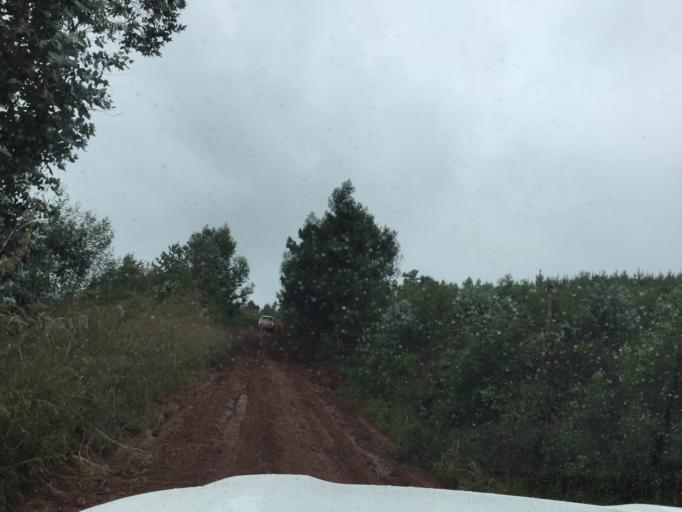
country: TZ
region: Iringa
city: Iringa
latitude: -8.1211
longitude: 35.8995
